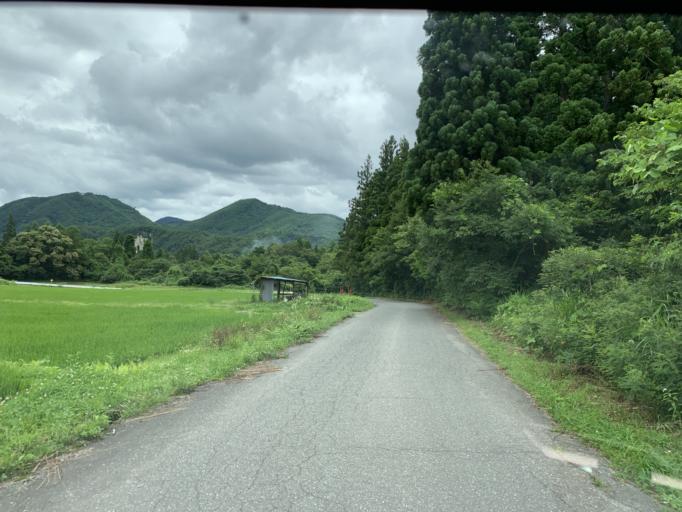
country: JP
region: Iwate
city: Ichinoseki
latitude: 38.9719
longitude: 140.9289
